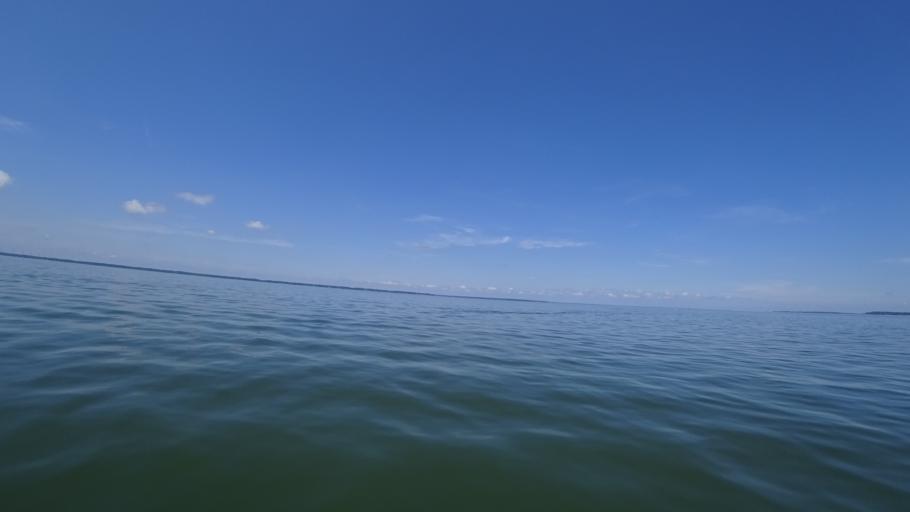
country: US
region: Virginia
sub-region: City of Newport News
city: Newport News
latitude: 37.0064
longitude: -76.4792
